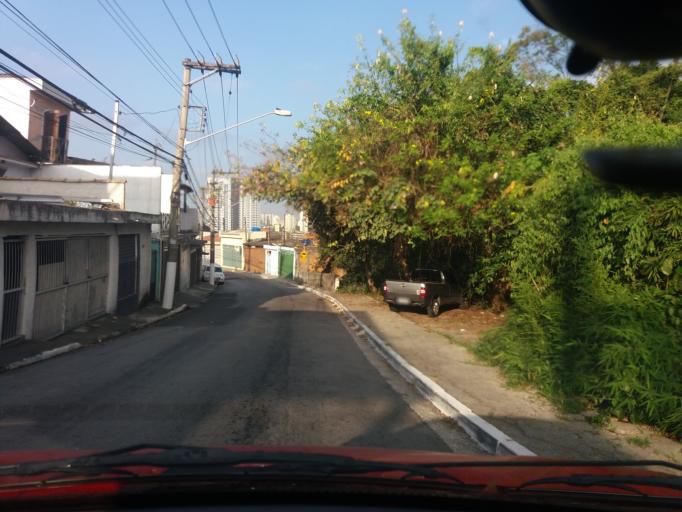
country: BR
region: Sao Paulo
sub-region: Taboao Da Serra
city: Taboao da Serra
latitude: -23.5940
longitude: -46.7445
